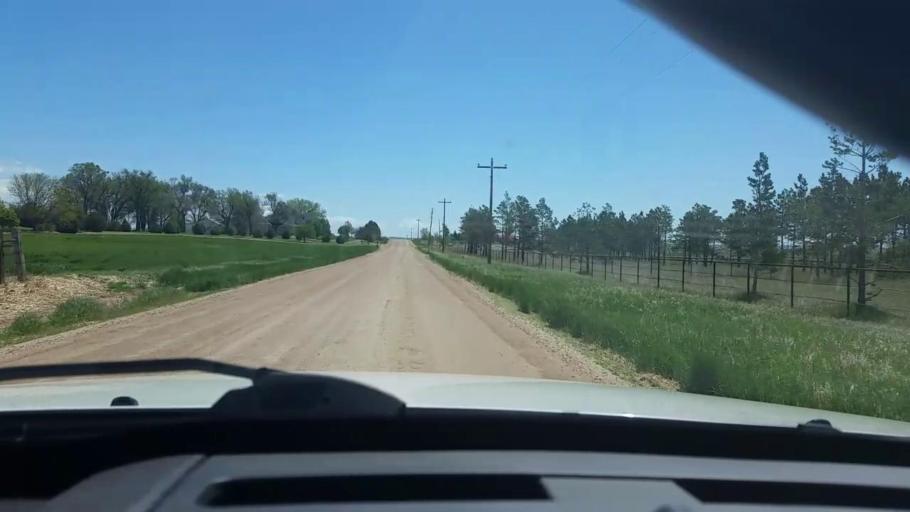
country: US
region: Colorado
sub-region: Larimer County
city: Wellington
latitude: 40.7981
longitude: -105.0596
